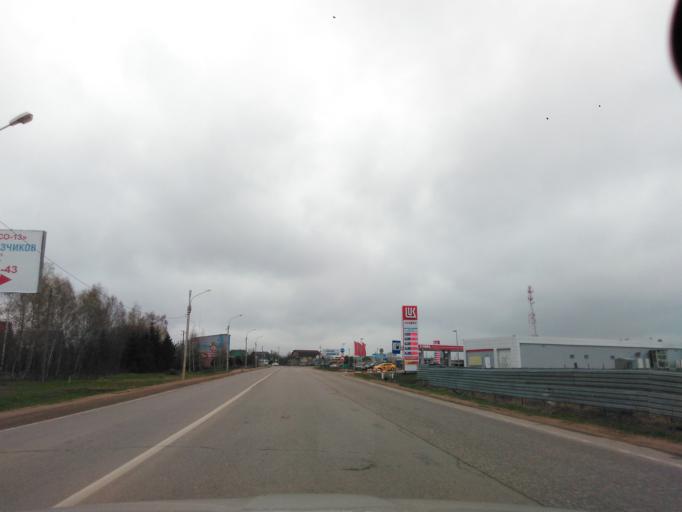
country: RU
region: Moskovskaya
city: Pavlovskaya Sloboda
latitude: 55.8165
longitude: 37.0700
